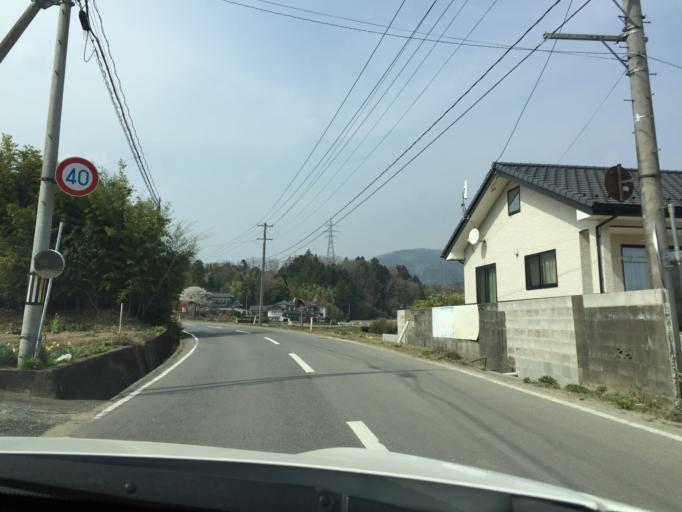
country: JP
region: Fukushima
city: Iwaki
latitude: 37.0215
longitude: 140.7310
